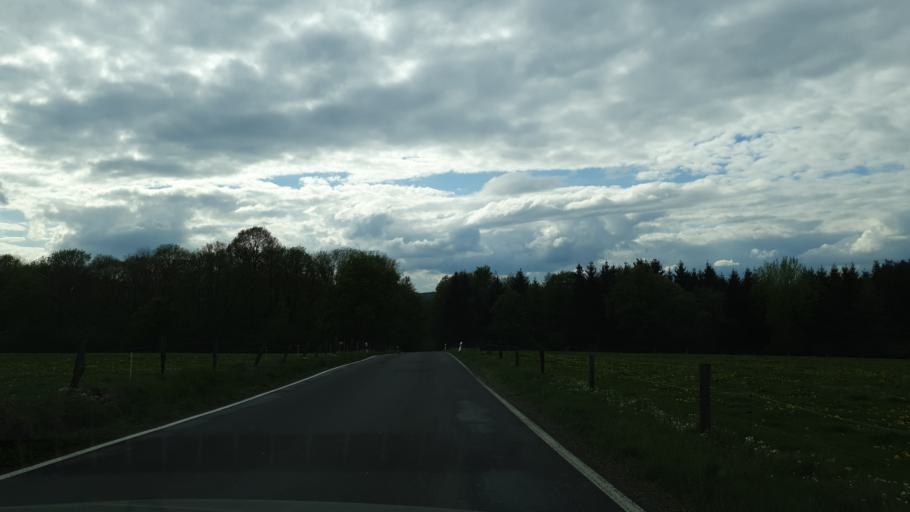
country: DE
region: Rheinland-Pfalz
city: Hardt
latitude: 50.6206
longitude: 7.9190
